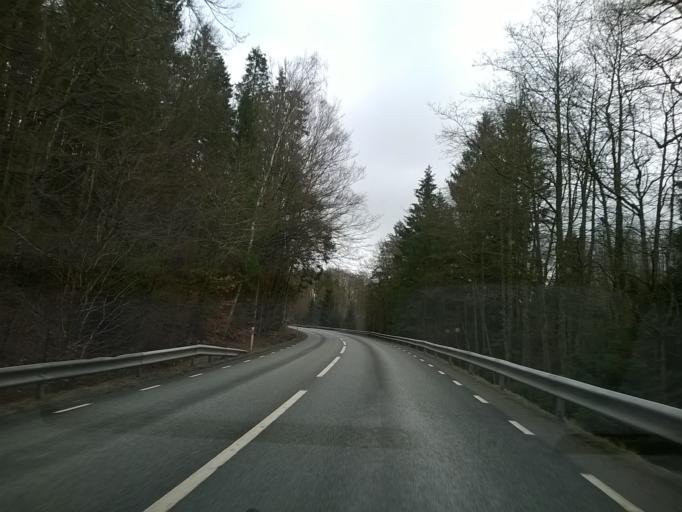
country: SE
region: Halland
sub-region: Varbergs Kommun
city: Tvaaker
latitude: 57.1501
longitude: 12.5941
